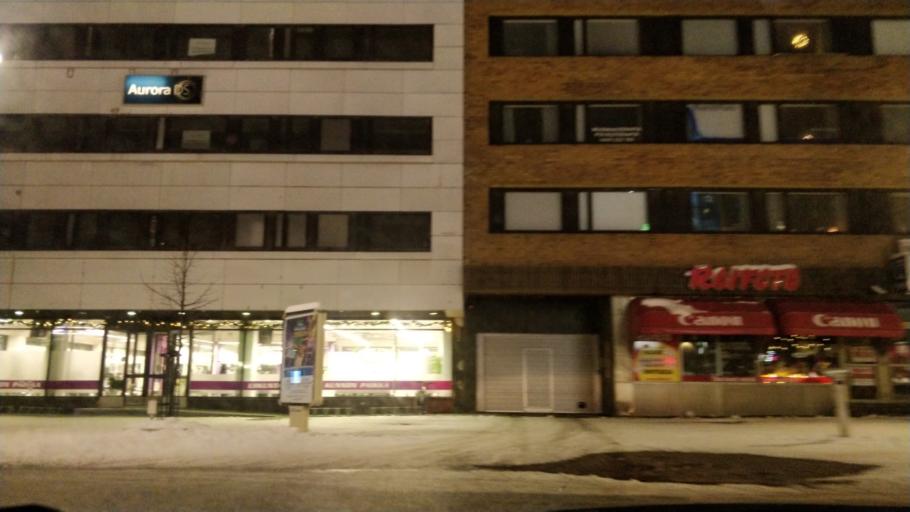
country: FI
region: Lapland
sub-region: Rovaniemi
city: Rovaniemi
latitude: 66.5020
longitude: 25.7280
